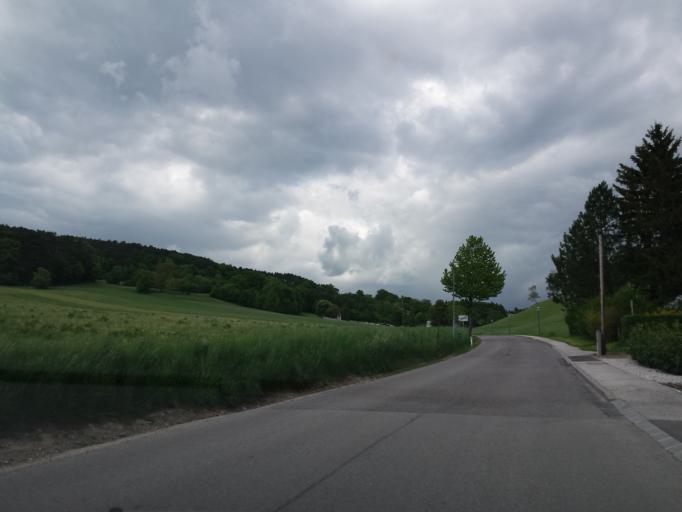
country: AT
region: Lower Austria
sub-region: Politischer Bezirk Baden
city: Hernstein
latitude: 47.8959
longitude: 16.1091
